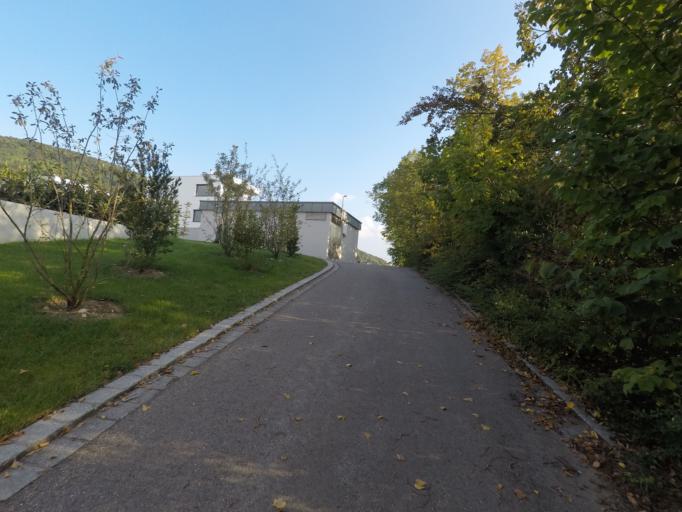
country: DE
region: Baden-Wuerttemberg
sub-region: Tuebingen Region
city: Pfullingen
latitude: 48.4678
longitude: 9.2358
